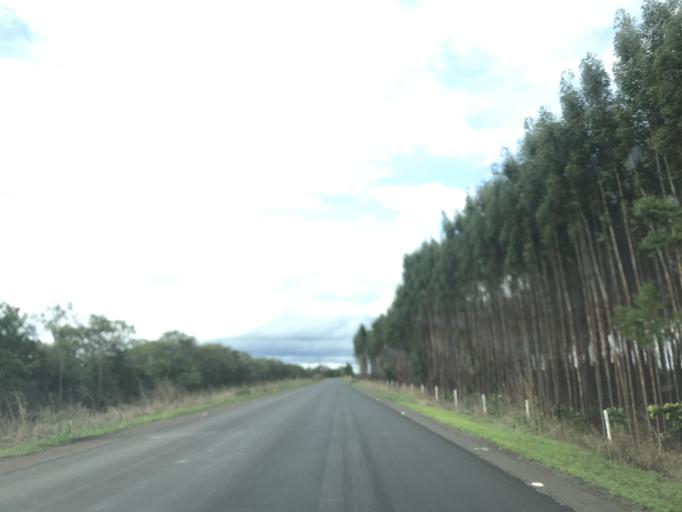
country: BR
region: Goias
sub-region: Bela Vista De Goias
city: Bela Vista de Goias
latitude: -16.9860
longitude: -48.6686
